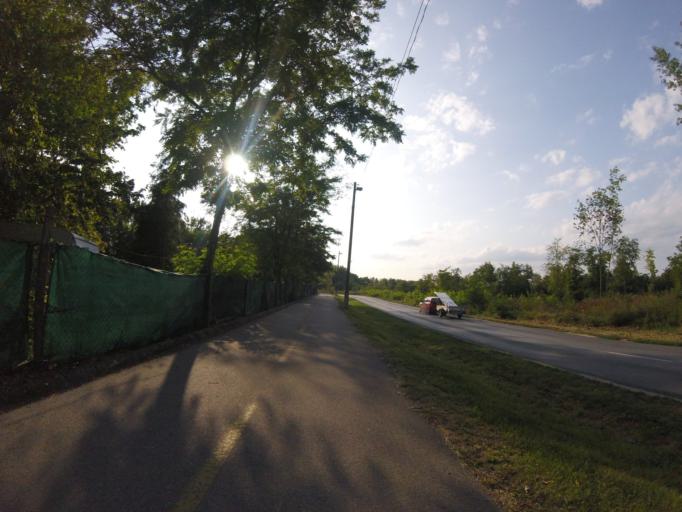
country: HU
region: Gyor-Moson-Sopron
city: Fertod
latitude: 47.6214
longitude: 16.7848
